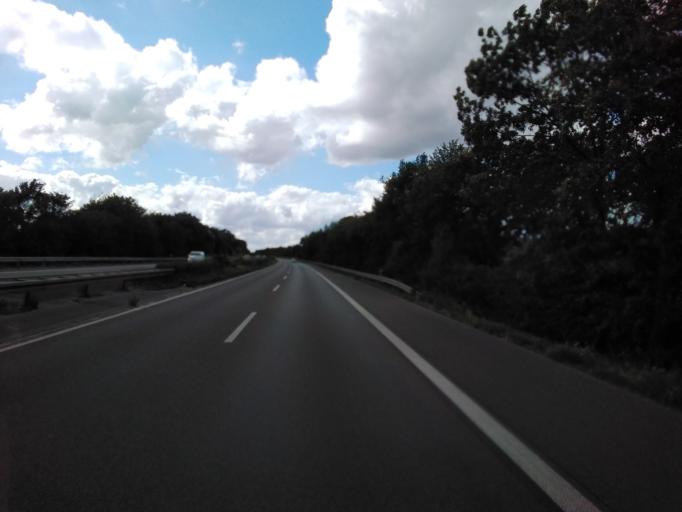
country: DE
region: North Rhine-Westphalia
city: Rheinberg
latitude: 51.5458
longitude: 6.5619
